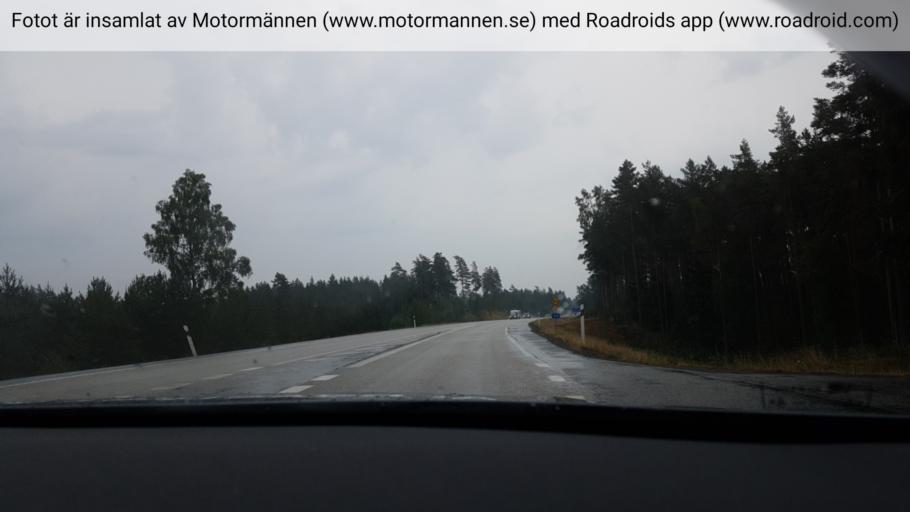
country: SE
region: Joenkoeping
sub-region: Jonkopings Kommun
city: Odensjo
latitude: 57.6164
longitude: 14.2026
